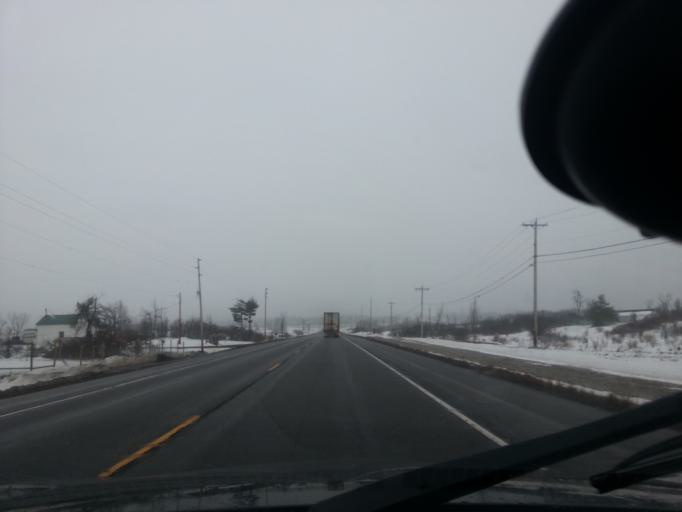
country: US
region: New York
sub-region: Jefferson County
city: Fort Drum
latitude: 44.0914
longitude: -75.7870
